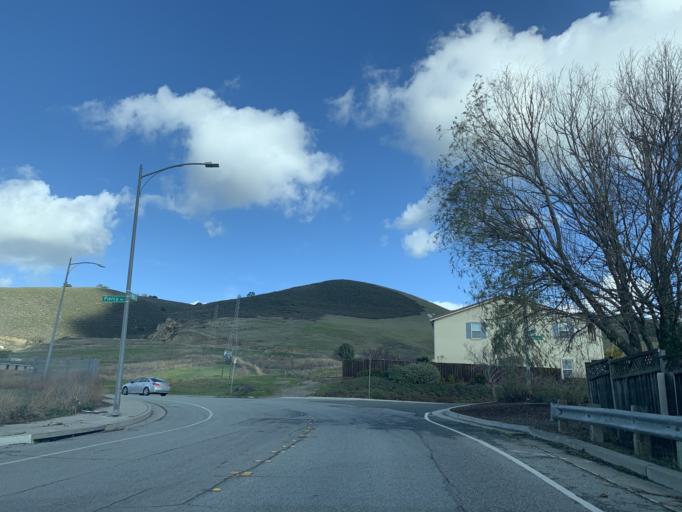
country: US
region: California
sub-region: Santa Clara County
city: Seven Trees
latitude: 37.2518
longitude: -121.7692
